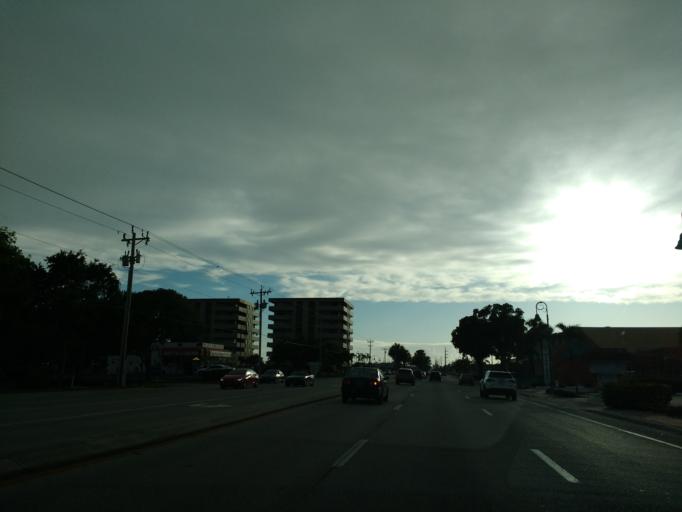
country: US
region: Florida
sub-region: Lee County
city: Cape Coral
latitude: 26.5627
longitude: -81.9621
